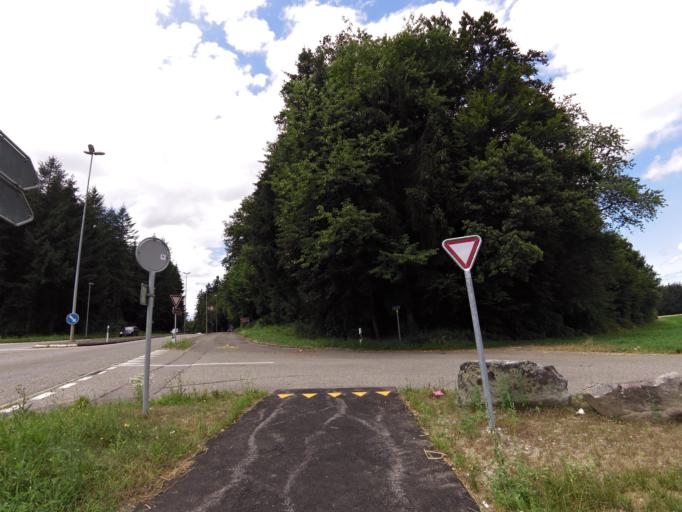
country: CH
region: Bern
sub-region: Oberaargau
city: Aarwangen
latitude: 47.2473
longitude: 7.7556
